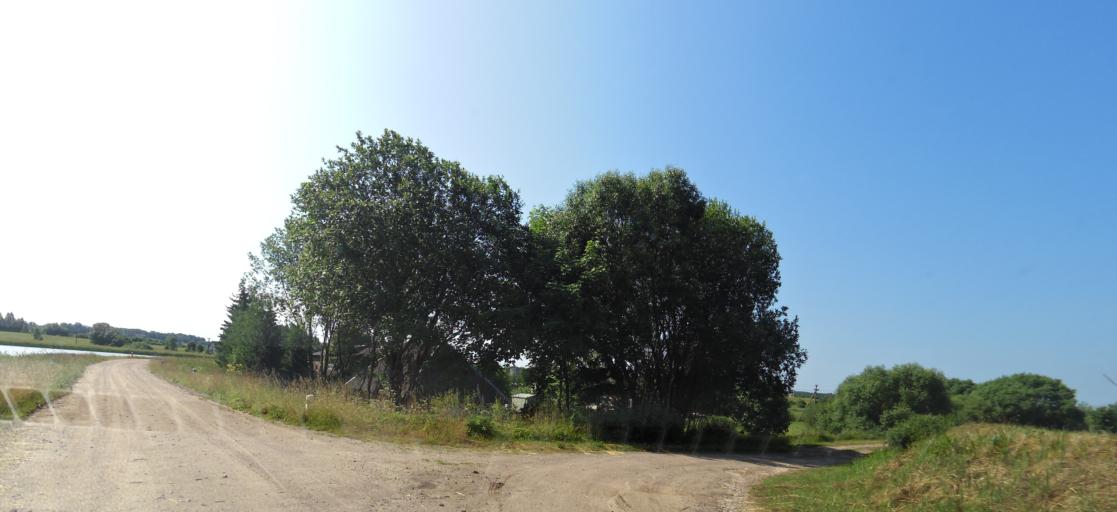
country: LT
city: Grigiskes
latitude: 54.8655
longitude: 25.0611
